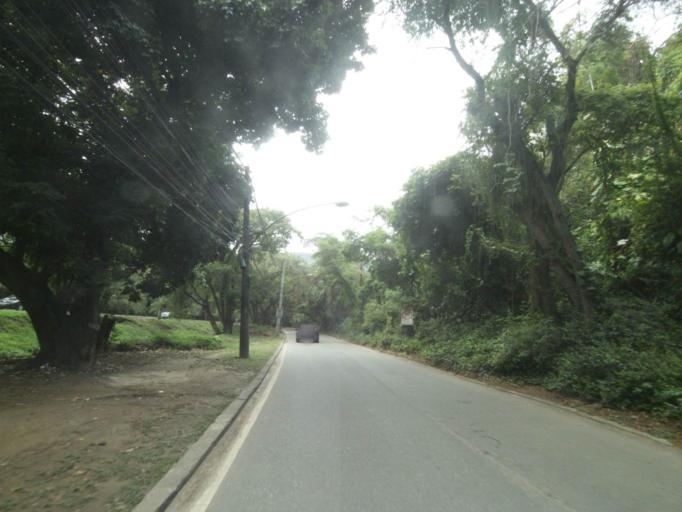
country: BR
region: Rio de Janeiro
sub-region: Rio De Janeiro
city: Rio de Janeiro
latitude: -22.9977
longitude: -43.3046
